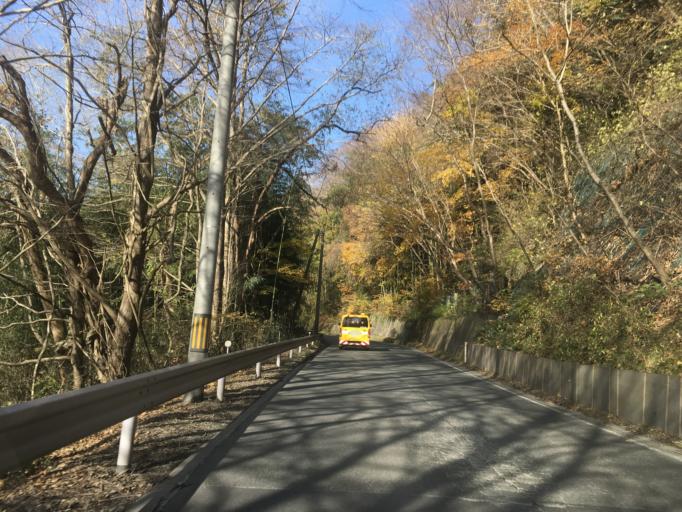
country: JP
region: Iwate
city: Ichinoseki
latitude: 38.9484
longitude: 141.2096
